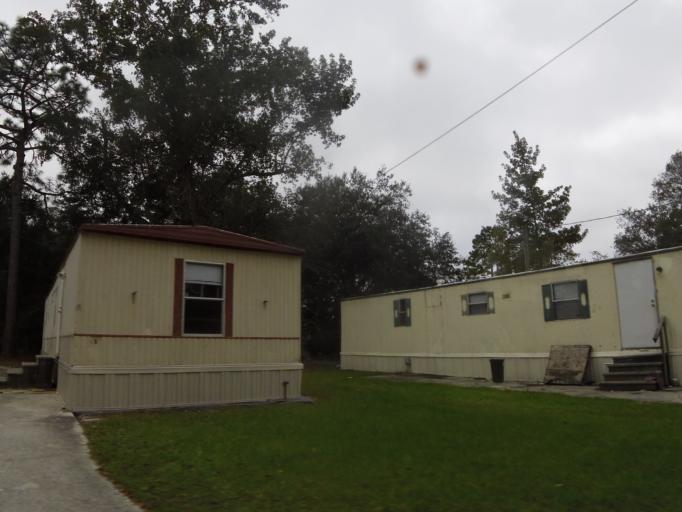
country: US
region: Florida
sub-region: Clay County
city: Bellair-Meadowbrook Terrace
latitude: 30.2450
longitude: -81.8274
